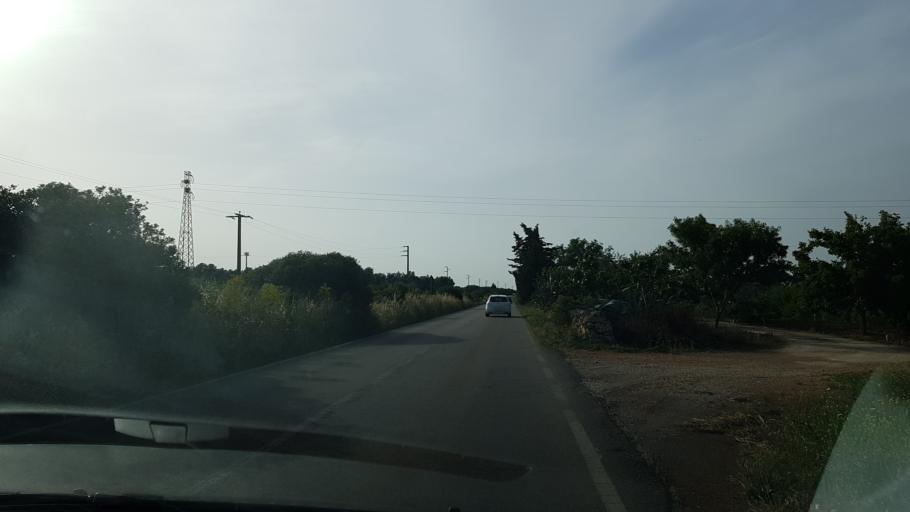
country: IT
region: Apulia
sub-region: Provincia di Lecce
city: Porto Cesareo
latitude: 40.3213
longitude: 17.8573
